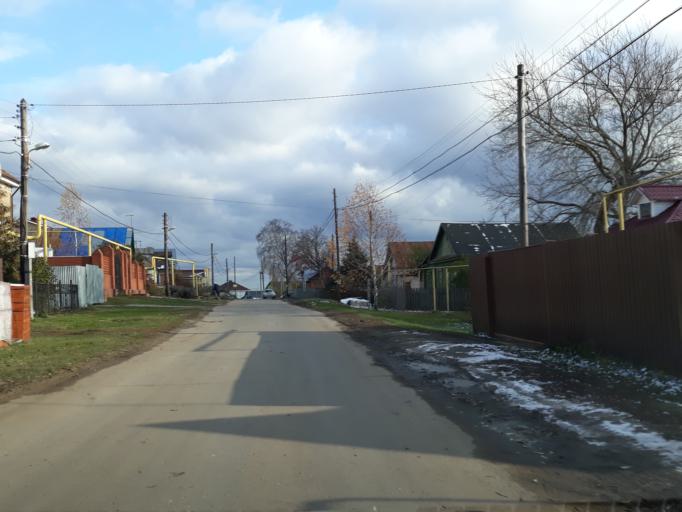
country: RU
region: Nizjnij Novgorod
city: Afonino
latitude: 56.2313
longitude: 44.0098
